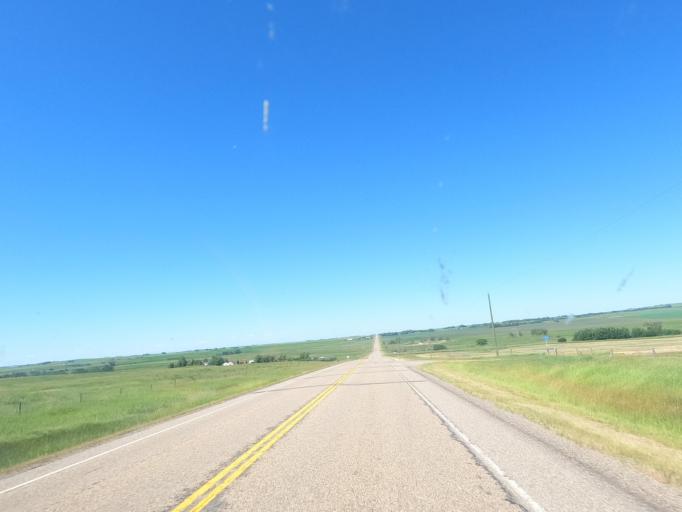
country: CA
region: Alberta
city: Strathmore
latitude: 51.1544
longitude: -113.2915
